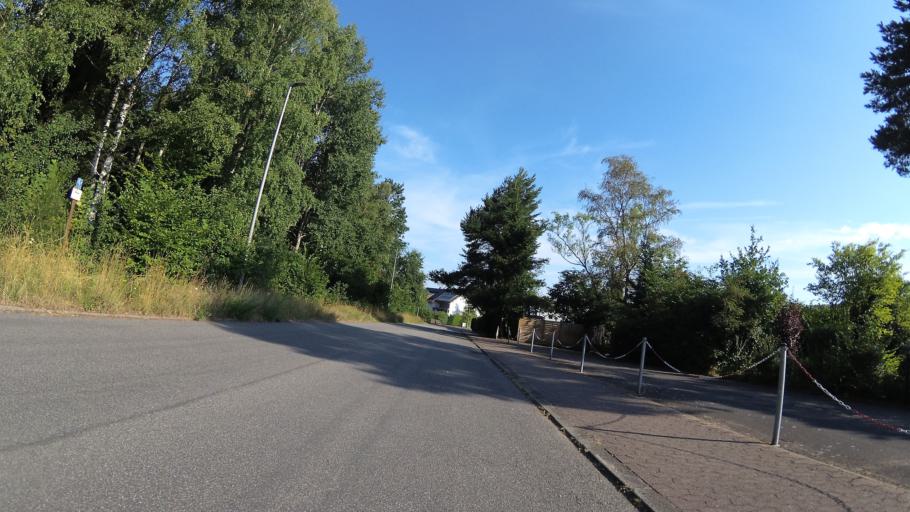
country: DE
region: Saarland
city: Homburg
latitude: 49.3369
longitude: 7.3183
